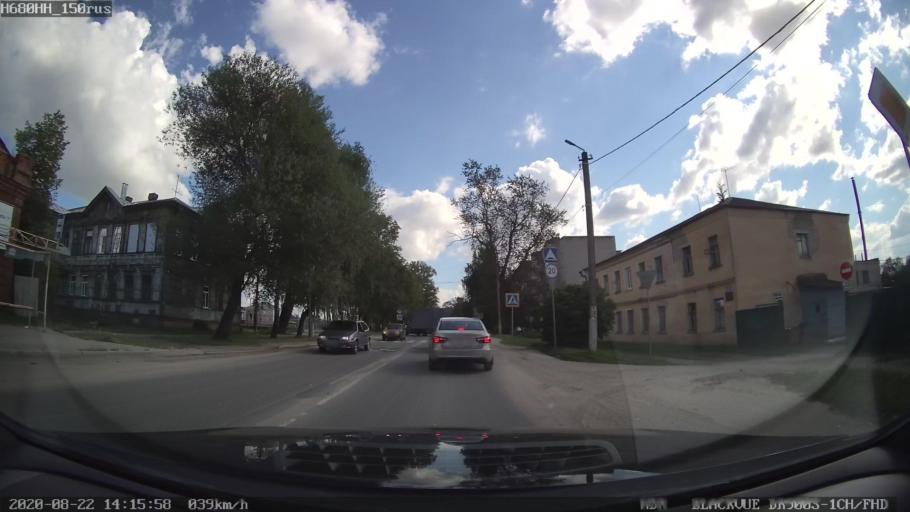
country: RU
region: Tverskaya
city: Bezhetsk
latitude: 57.7773
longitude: 36.6962
